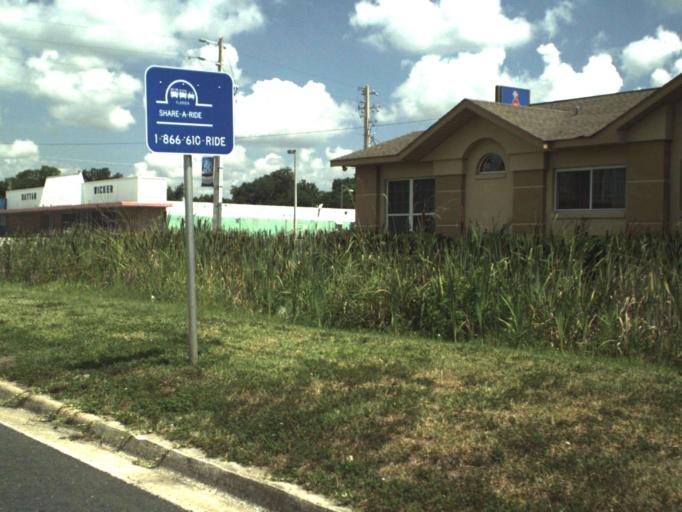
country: US
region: Florida
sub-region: Lake County
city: Leesburg
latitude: 28.8162
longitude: -81.8748
